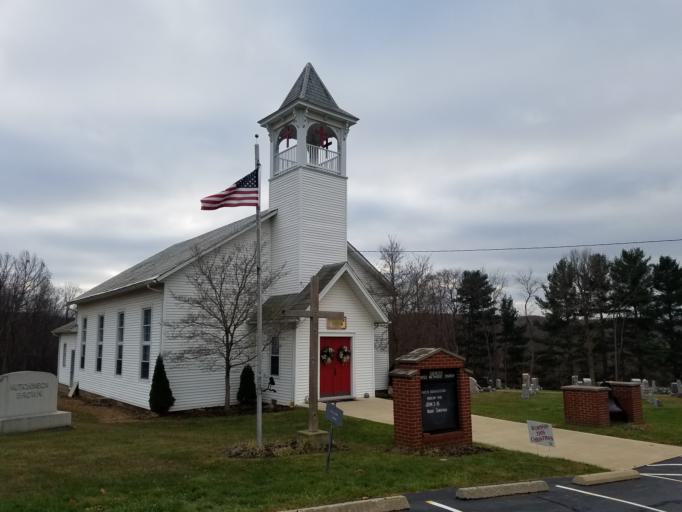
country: US
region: Ohio
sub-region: Knox County
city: Mount Vernon
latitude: 40.4491
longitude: -82.4359
